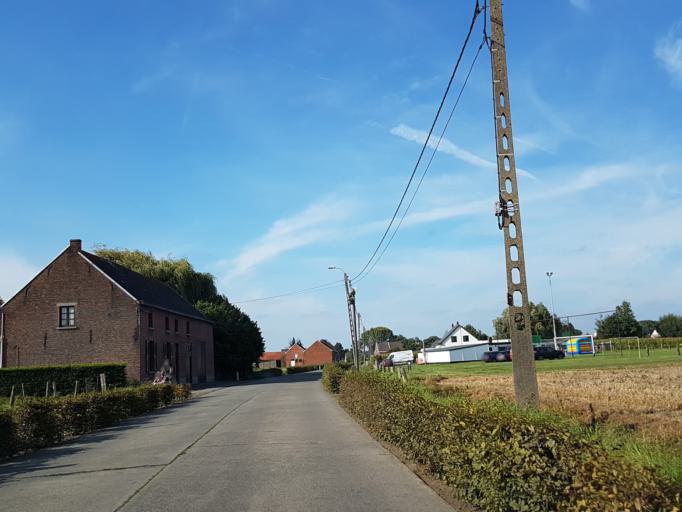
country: BE
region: Flanders
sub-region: Provincie Vlaams-Brabant
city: Zemst
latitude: 50.9999
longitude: 4.4258
